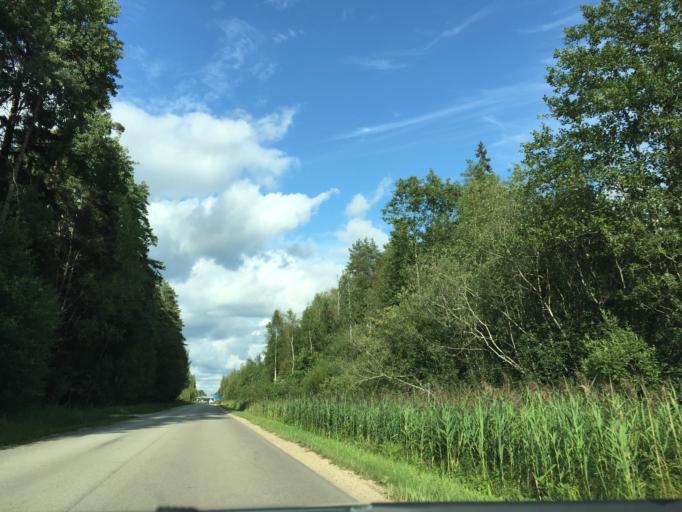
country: LV
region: Ogre
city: Ogre
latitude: 56.8387
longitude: 24.6633
